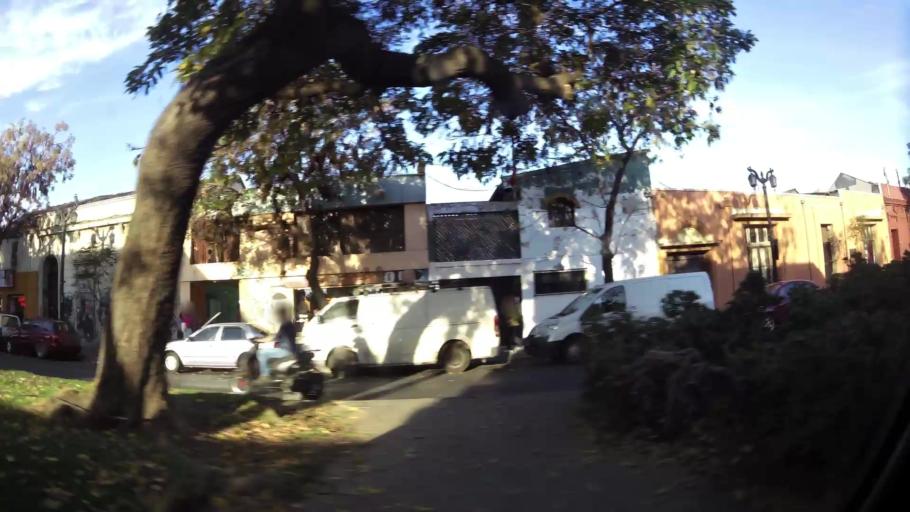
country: CL
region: Santiago Metropolitan
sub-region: Provincia de Santiago
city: Santiago
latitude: -33.4375
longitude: -70.6687
